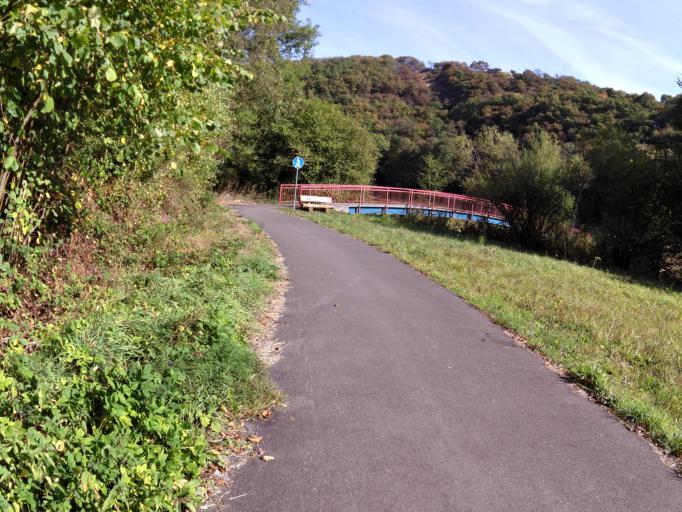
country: DE
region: Rheinland-Pfalz
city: Niederraden
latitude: 49.9859
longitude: 6.3130
